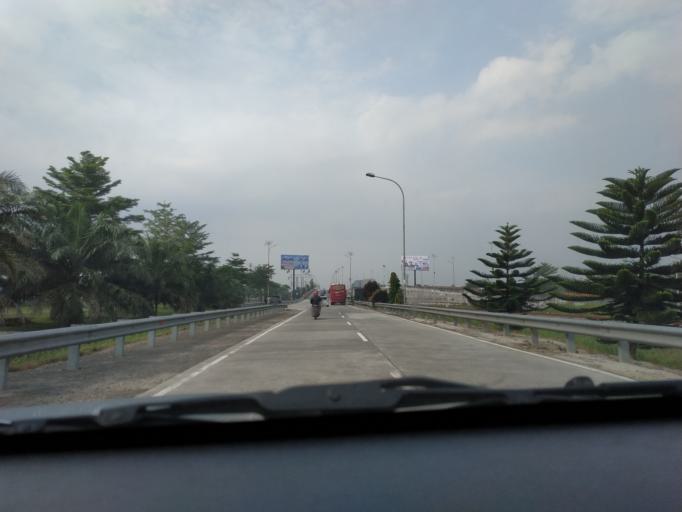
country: ID
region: North Sumatra
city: Percut
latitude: 3.6121
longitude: 98.8561
